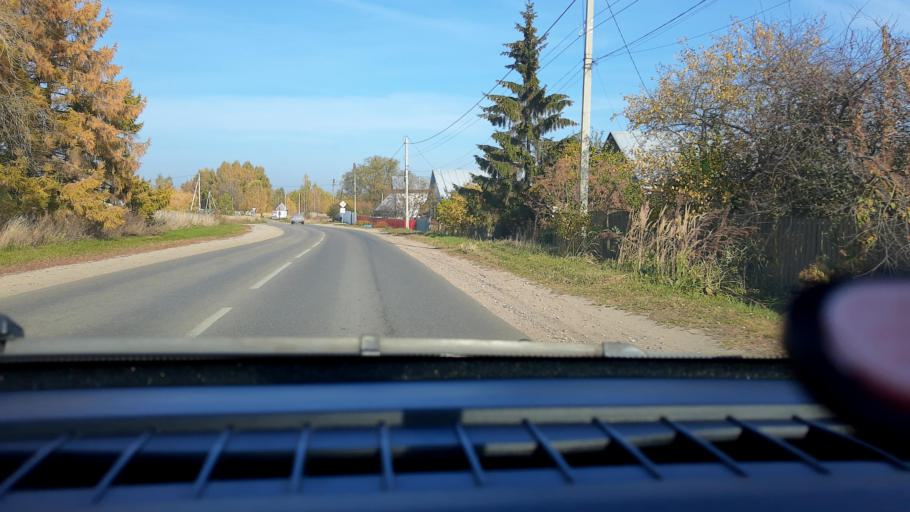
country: RU
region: Nizjnij Novgorod
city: Kstovo
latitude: 56.1513
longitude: 44.2319
